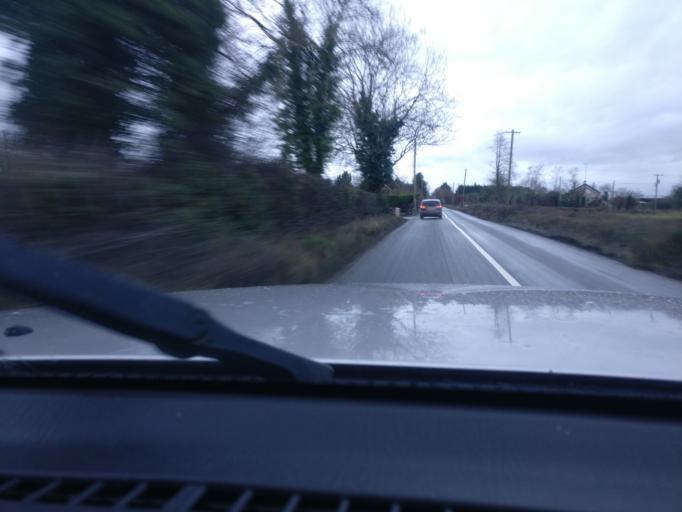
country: IE
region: Leinster
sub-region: An Mhi
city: Longwood
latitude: 53.4694
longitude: -6.9097
